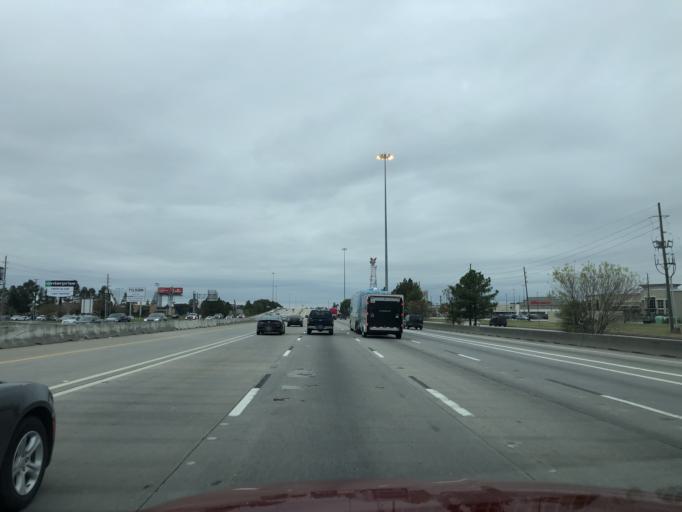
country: US
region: Texas
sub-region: Harris County
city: Spring
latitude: 30.0582
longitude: -95.4331
